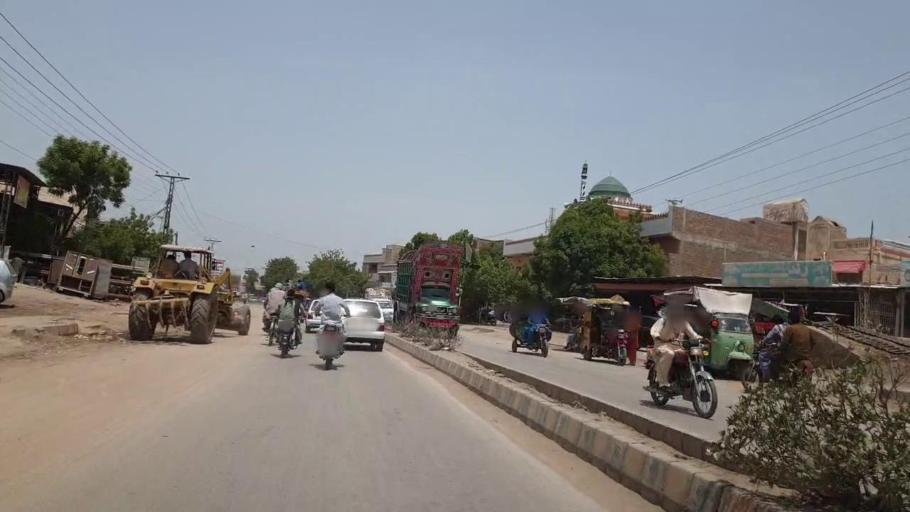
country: PK
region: Sindh
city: Nawabshah
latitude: 26.2522
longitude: 68.4244
